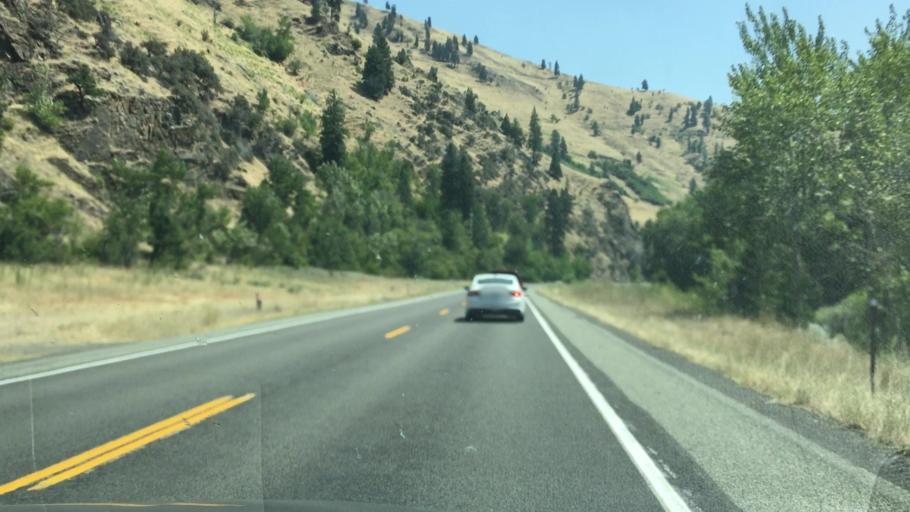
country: US
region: Idaho
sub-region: Valley County
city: McCall
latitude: 45.2842
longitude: -116.3500
